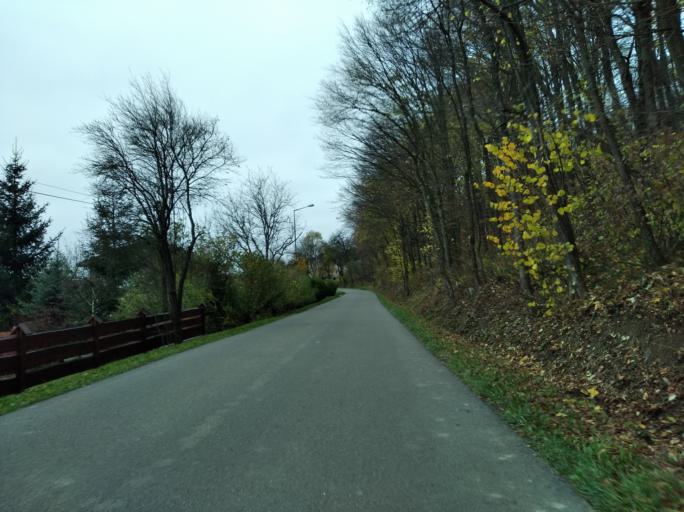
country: PL
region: Subcarpathian Voivodeship
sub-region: Powiat strzyzowski
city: Frysztak
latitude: 49.8318
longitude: 21.6304
